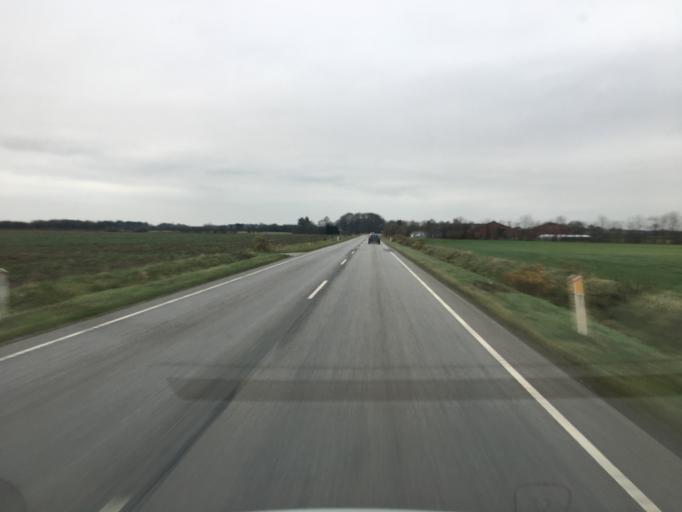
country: DK
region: South Denmark
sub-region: Aabenraa Kommune
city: Tinglev
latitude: 54.9787
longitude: 9.1534
